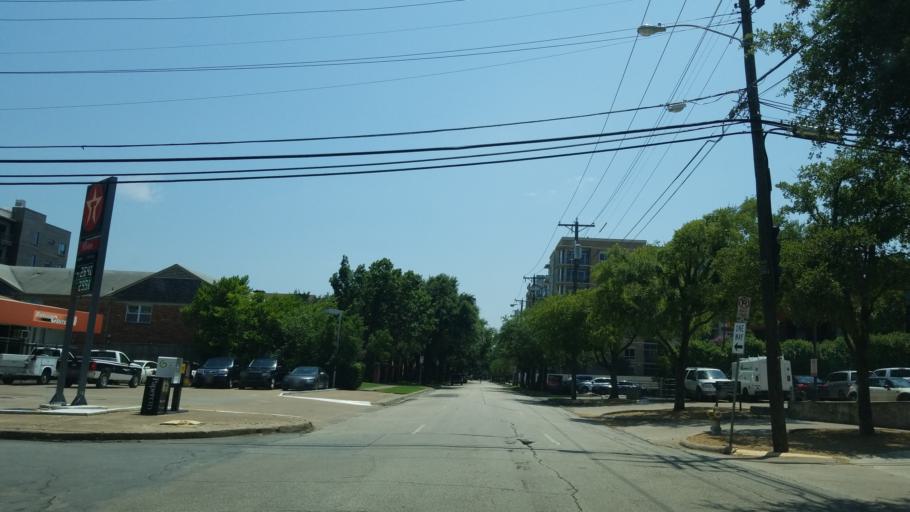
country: US
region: Texas
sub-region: Dallas County
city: Highland Park
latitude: 32.8274
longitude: -96.7865
